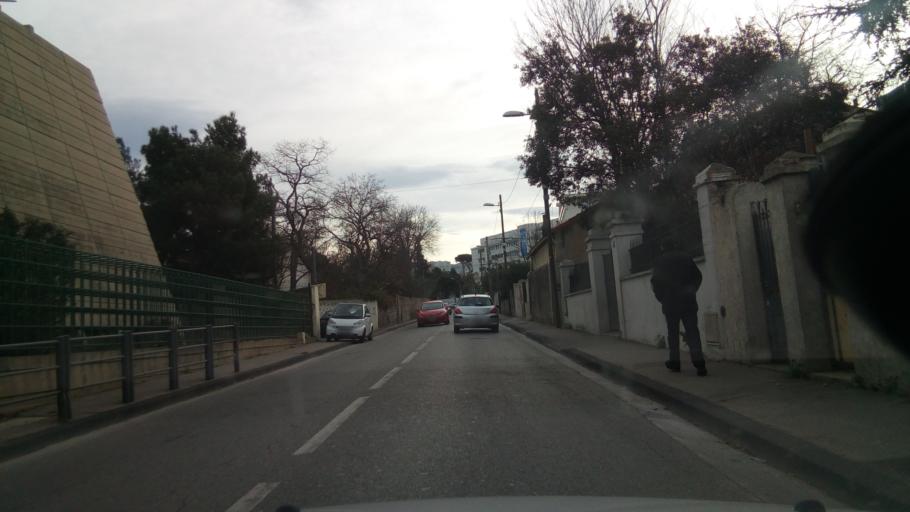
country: FR
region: Provence-Alpes-Cote d'Azur
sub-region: Departement des Bouches-du-Rhone
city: Marseille 09
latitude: 43.2647
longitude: 5.4095
